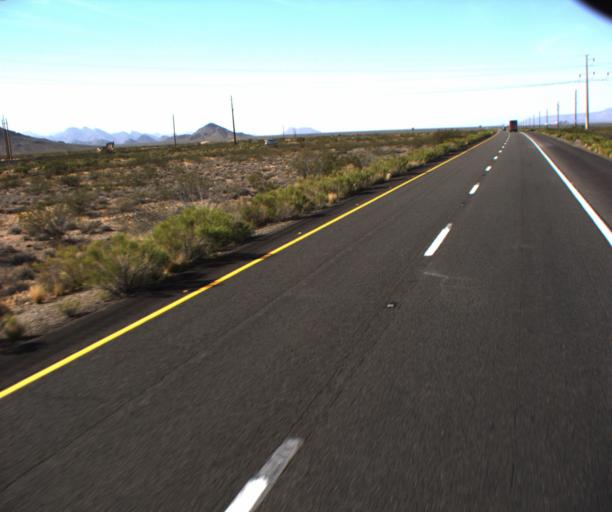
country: US
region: Arizona
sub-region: Mohave County
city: Kingman
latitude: 35.1077
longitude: -114.1169
